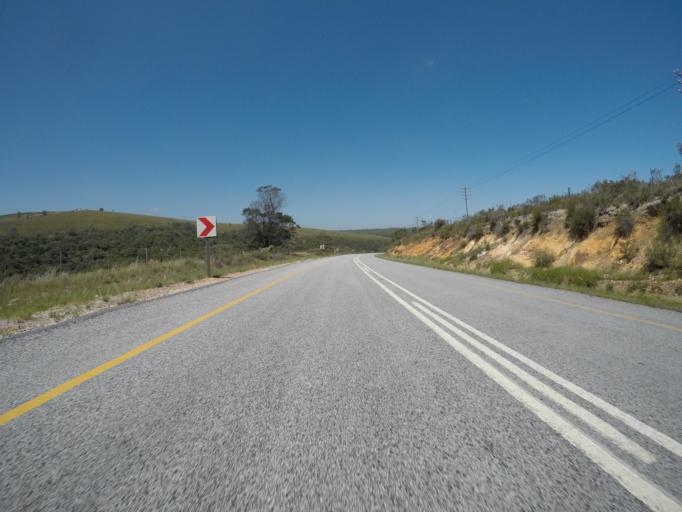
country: ZA
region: Eastern Cape
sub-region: Cacadu District Municipality
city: Kruisfontein
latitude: -34.0197
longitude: 24.5847
